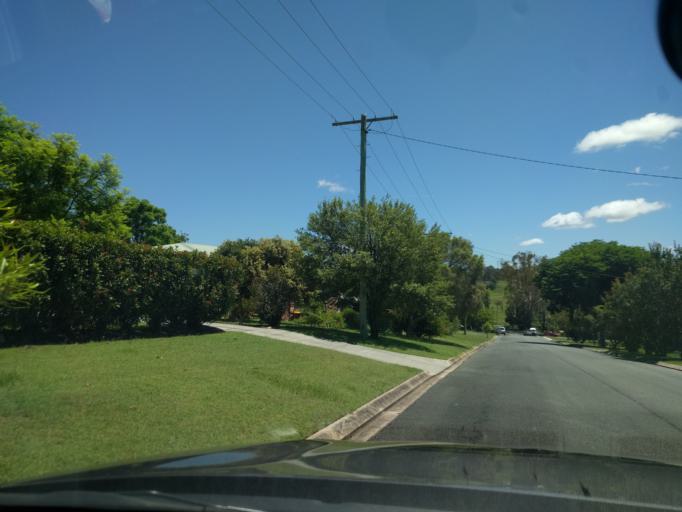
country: AU
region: Queensland
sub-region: Logan
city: Cedar Vale
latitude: -27.9866
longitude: 153.0050
